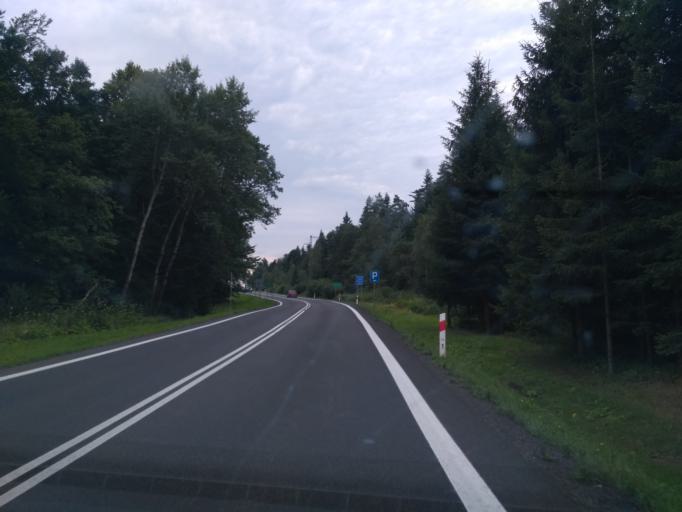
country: PL
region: Subcarpathian Voivodeship
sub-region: Powiat sanocki
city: Zagorz
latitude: 49.5072
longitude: 22.2940
